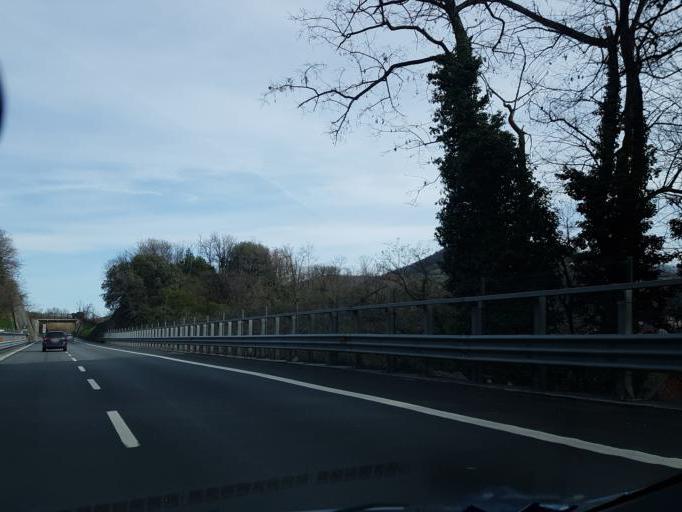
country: IT
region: Liguria
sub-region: Provincia di Genova
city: Manesseno
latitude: 44.4816
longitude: 8.9179
